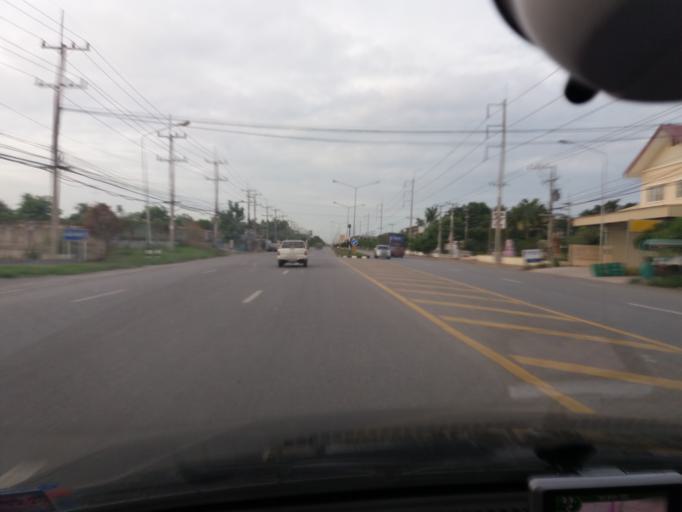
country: TH
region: Suphan Buri
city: U Thong
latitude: 14.3986
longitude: 99.8960
